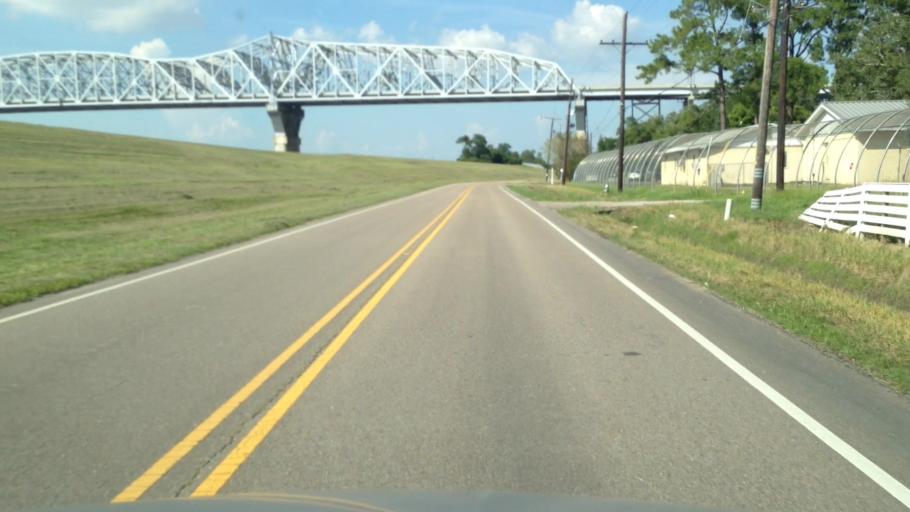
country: US
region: Louisiana
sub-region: Jefferson Parish
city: Bridge City
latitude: 29.9379
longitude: -90.1694
